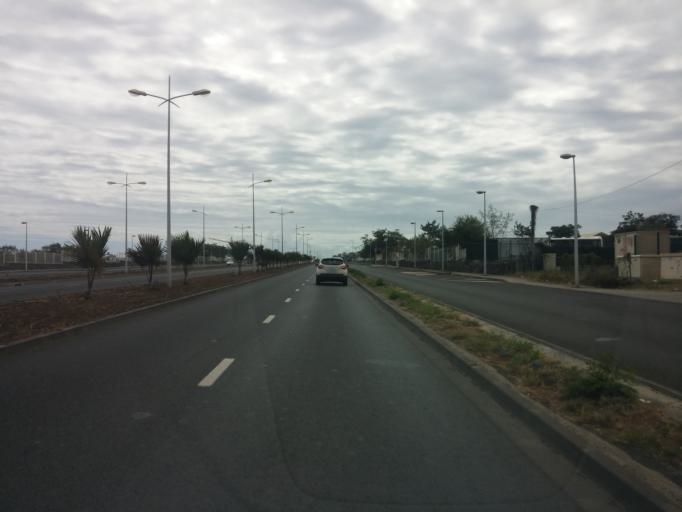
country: RE
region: Reunion
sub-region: Reunion
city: Le Port
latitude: -20.9680
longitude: 55.2954
